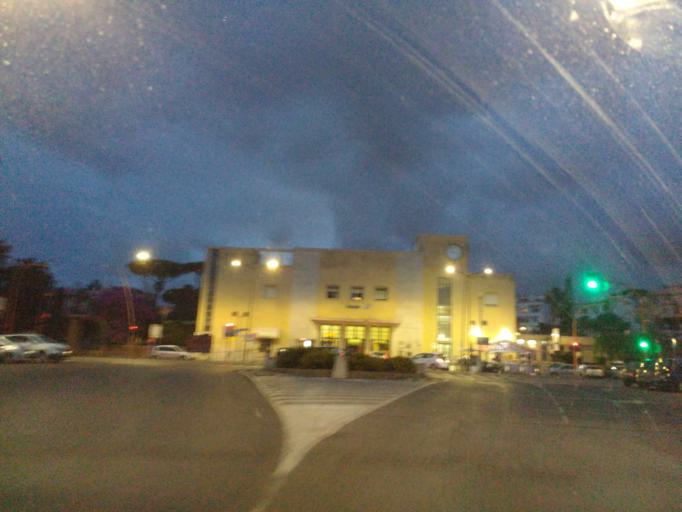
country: IT
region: Latium
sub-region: Citta metropolitana di Roma Capitale
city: Anzio
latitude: 41.4514
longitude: 12.6296
